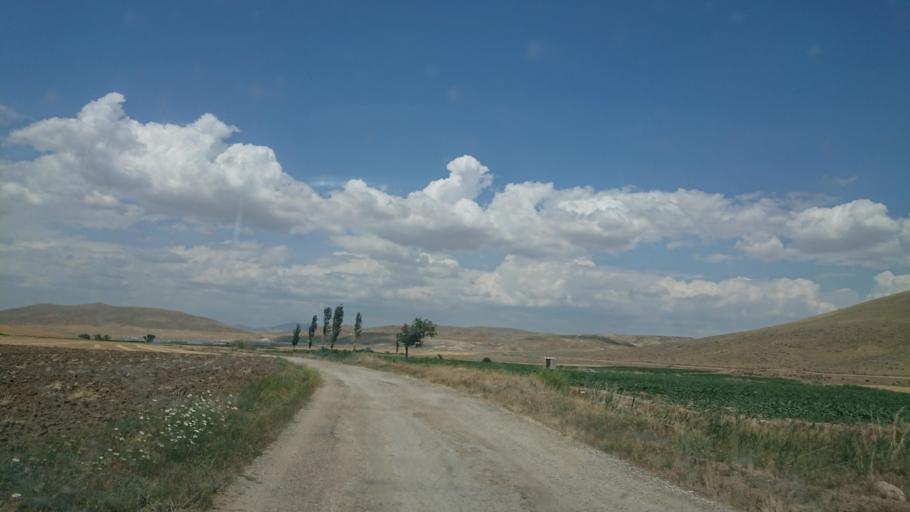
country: TR
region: Aksaray
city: Sariyahsi
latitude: 38.9862
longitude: 33.9080
